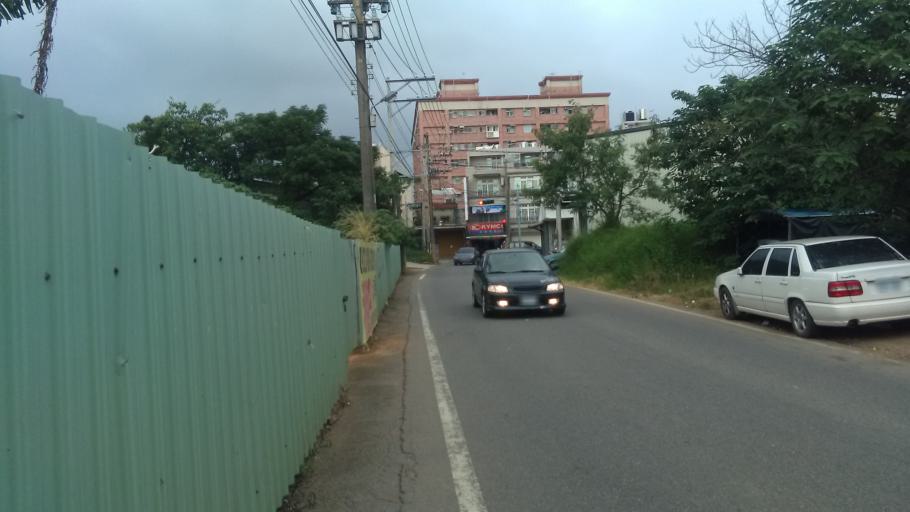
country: TW
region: Taiwan
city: Taoyuan City
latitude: 24.9555
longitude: 121.2615
